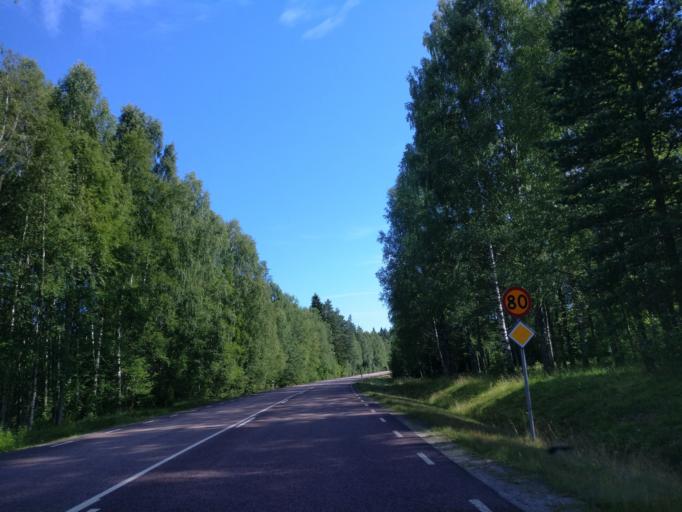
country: SE
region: Vaermland
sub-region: Hagfors Kommun
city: Hagfors
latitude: 60.0562
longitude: 13.7064
